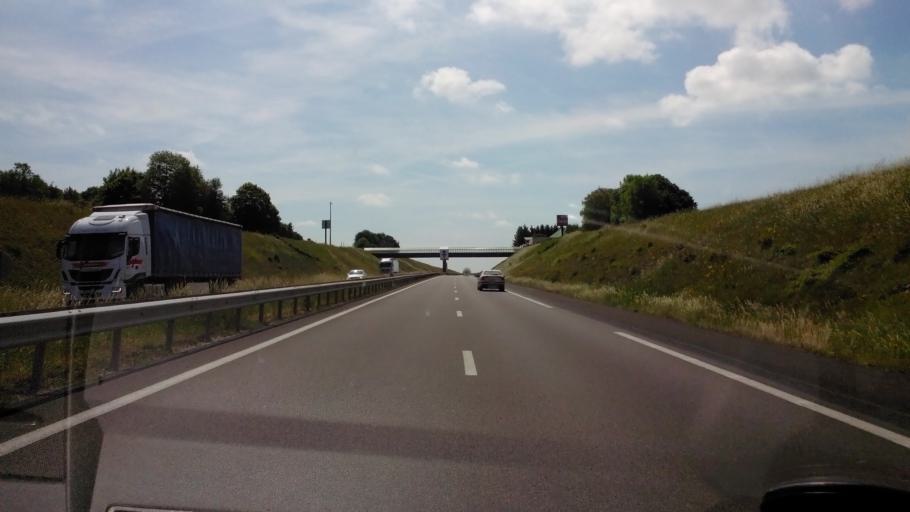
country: FR
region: Lorraine
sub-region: Departement des Vosges
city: Chatenois
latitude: 48.2704
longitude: 5.8601
